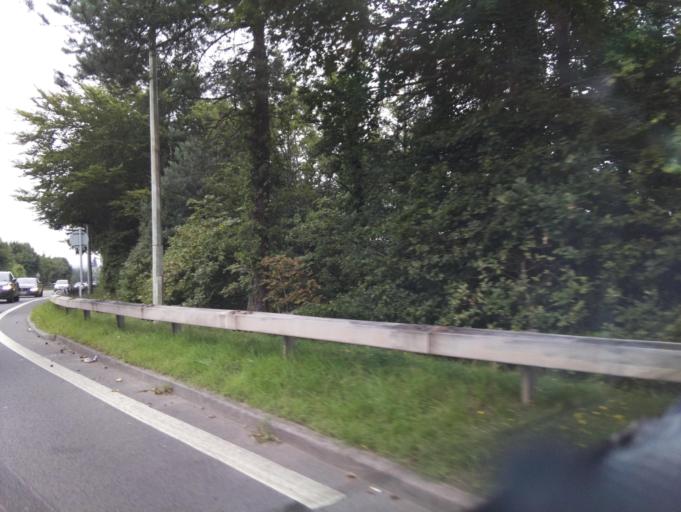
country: GB
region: England
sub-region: Shropshire
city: Hadley
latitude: 52.6898
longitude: -2.4885
